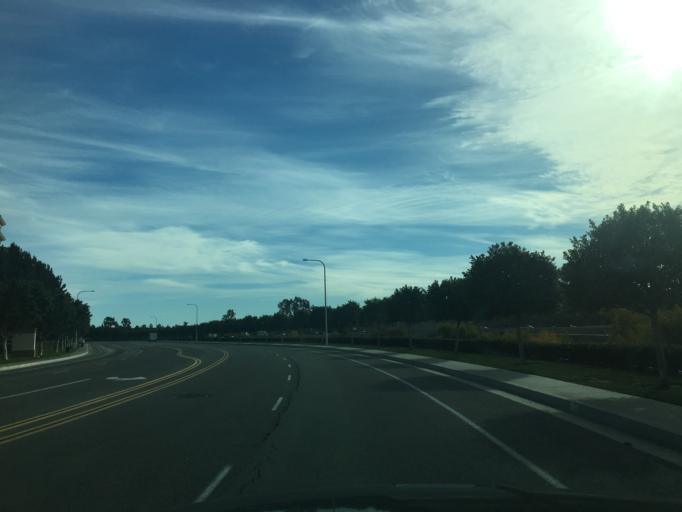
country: US
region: California
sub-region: Orange County
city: Laguna Woods
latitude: 33.6537
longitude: -117.7562
